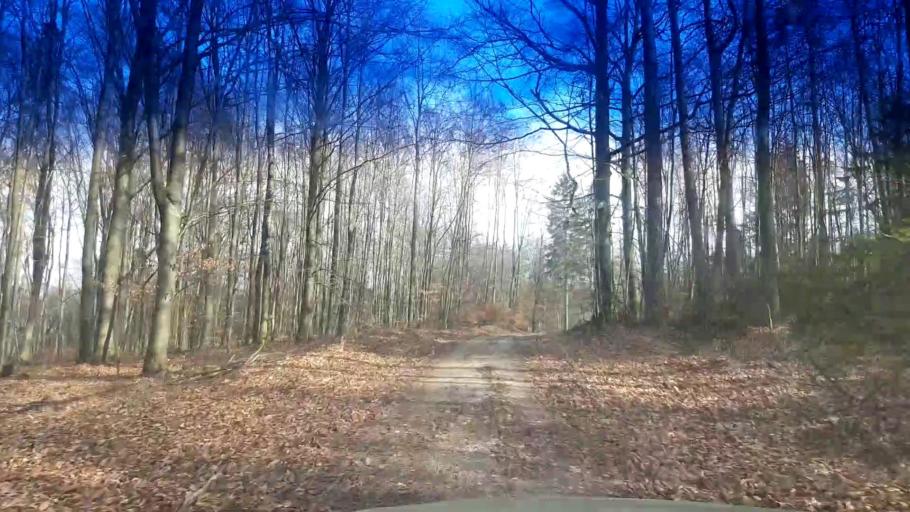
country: DE
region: Bavaria
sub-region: Upper Franconia
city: Schesslitz
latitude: 49.9366
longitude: 11.0480
